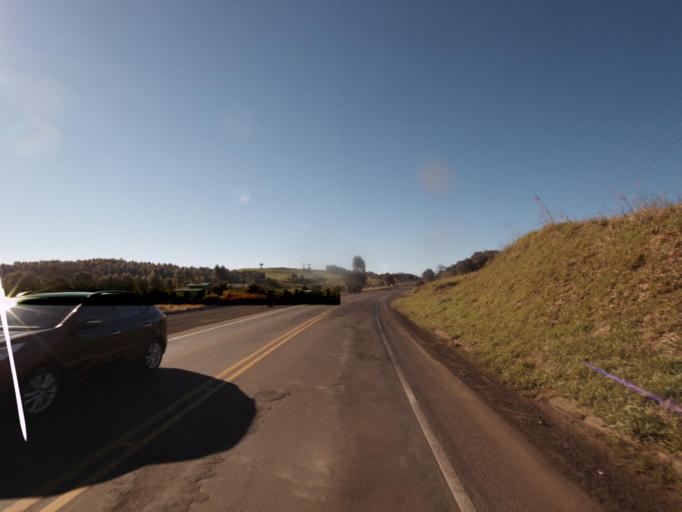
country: AR
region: Misiones
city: Bernardo de Irigoyen
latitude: -26.6148
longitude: -53.5193
